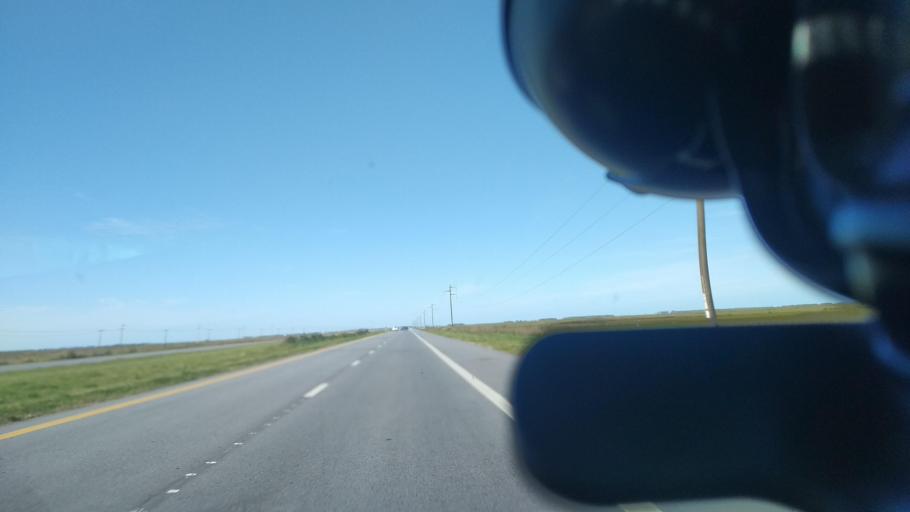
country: AR
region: Buenos Aires
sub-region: Partido de General Lavalle
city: General Lavalle
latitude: -36.4214
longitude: -56.8575
